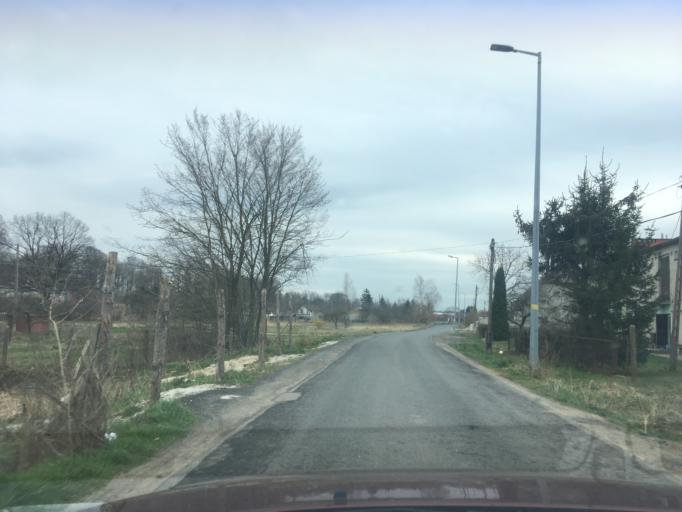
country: PL
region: Lower Silesian Voivodeship
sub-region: Powiat zgorzelecki
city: Lagow
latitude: 51.1647
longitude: 15.0392
